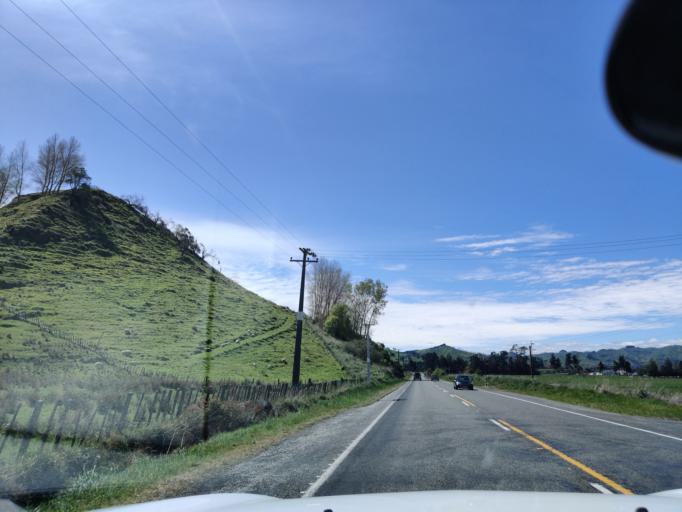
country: NZ
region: Manawatu-Wanganui
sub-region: Ruapehu District
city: Waiouru
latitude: -39.8508
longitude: 175.7325
